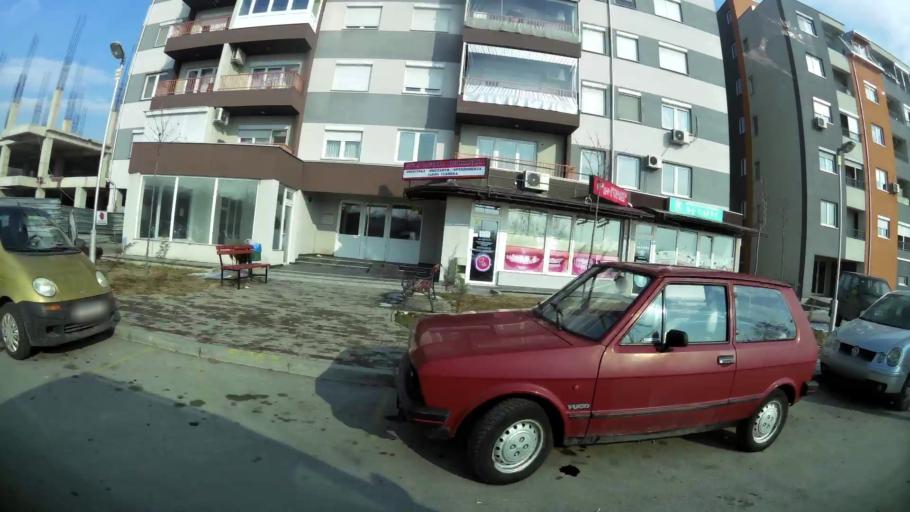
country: MK
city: Creshevo
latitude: 42.0057
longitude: 21.5011
